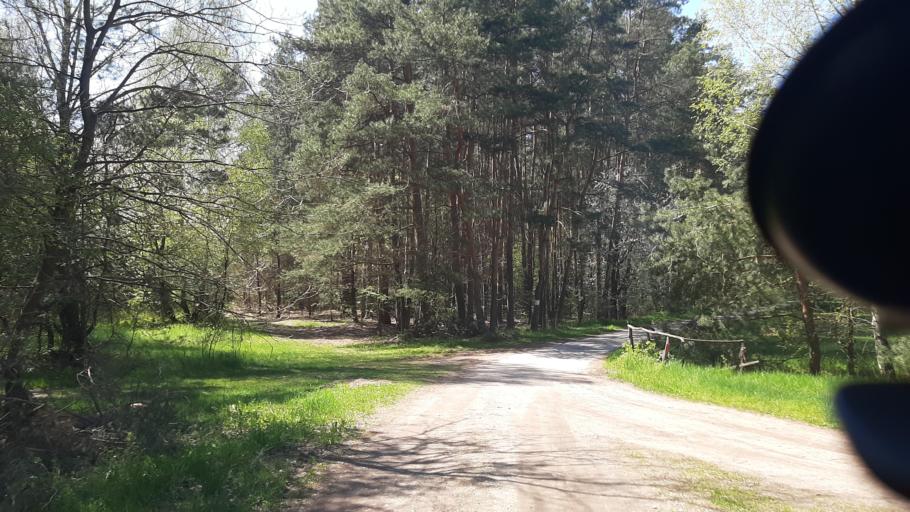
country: PL
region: Lublin Voivodeship
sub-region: Powiat lubartowski
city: Abramow
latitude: 51.4242
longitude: 22.2879
